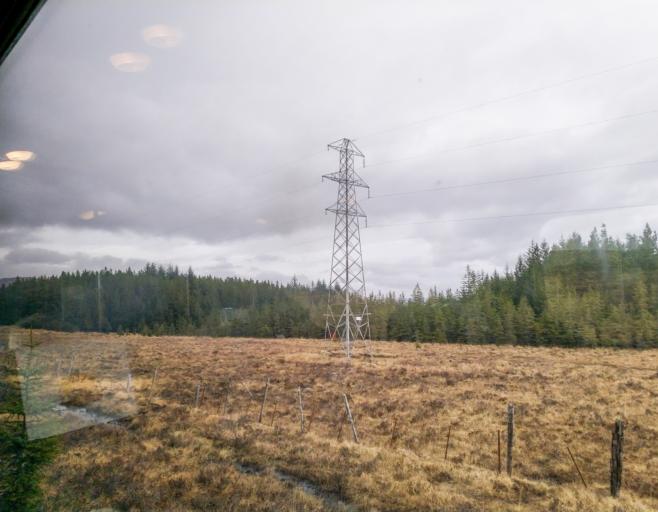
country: GB
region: Scotland
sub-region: Highland
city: Spean Bridge
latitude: 56.6634
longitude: -4.5645
